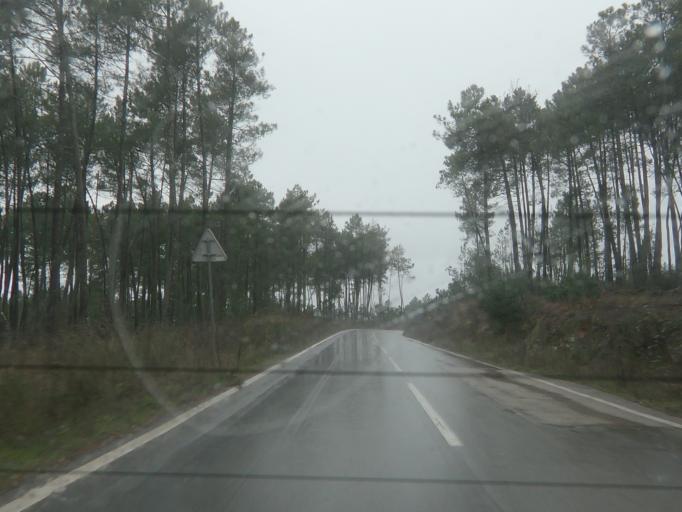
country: PT
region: Vila Real
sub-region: Sabrosa
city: Vilela
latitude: 41.2267
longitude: -7.6785
